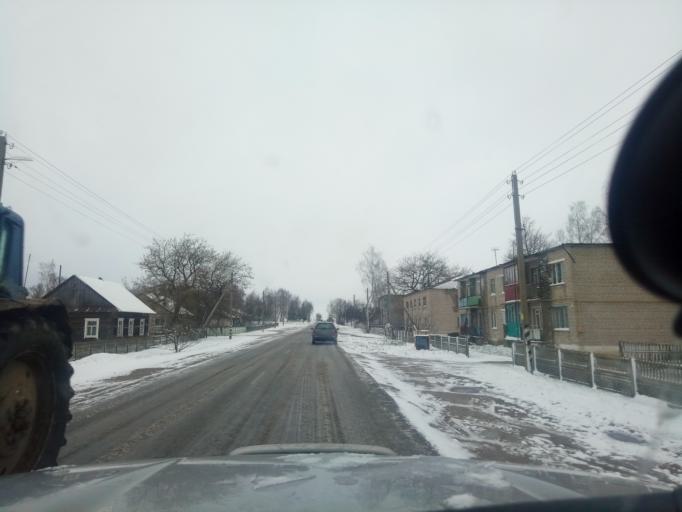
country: BY
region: Minsk
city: Klyetsk
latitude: 53.0512
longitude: 26.7486
